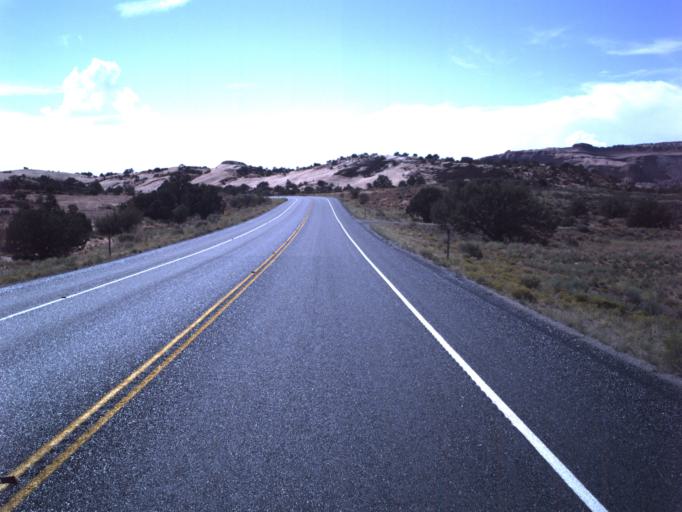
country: US
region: Utah
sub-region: Grand County
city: Moab
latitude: 38.6406
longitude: -109.7456
